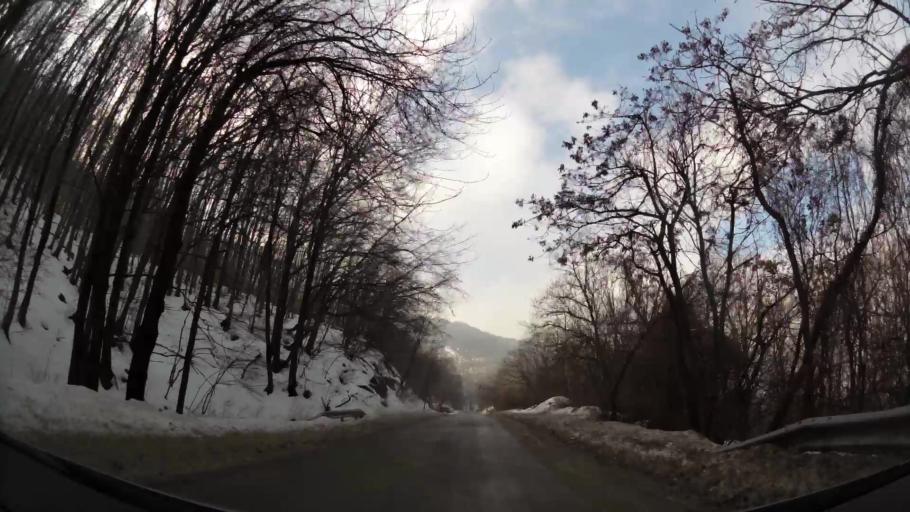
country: BG
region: Sofia-Capital
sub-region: Stolichna Obshtina
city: Sofia
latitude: 42.6435
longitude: 23.2338
